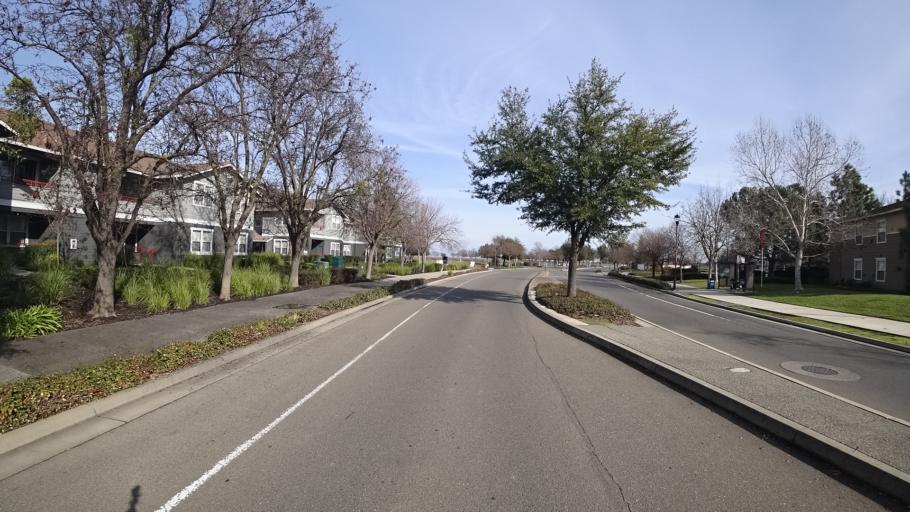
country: US
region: California
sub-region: Yolo County
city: Davis
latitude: 38.5587
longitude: -121.6969
